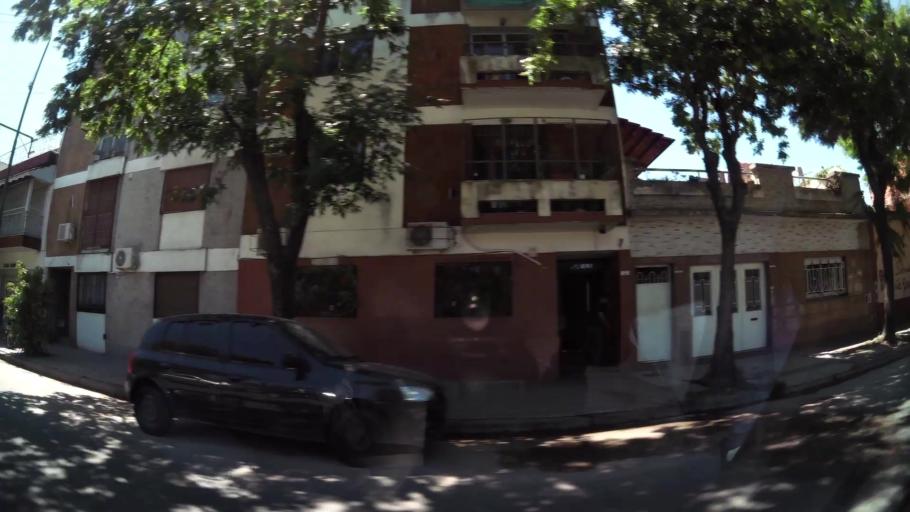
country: AR
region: Buenos Aires F.D.
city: Buenos Aires
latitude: -34.6423
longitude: -58.4092
